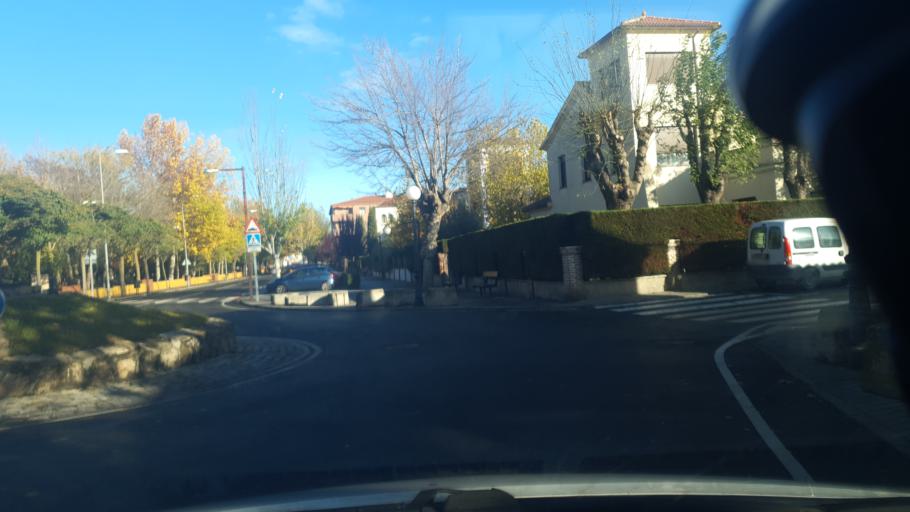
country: ES
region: Castille and Leon
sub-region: Provincia de Avila
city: Arevalo
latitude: 41.0569
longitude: -4.7207
